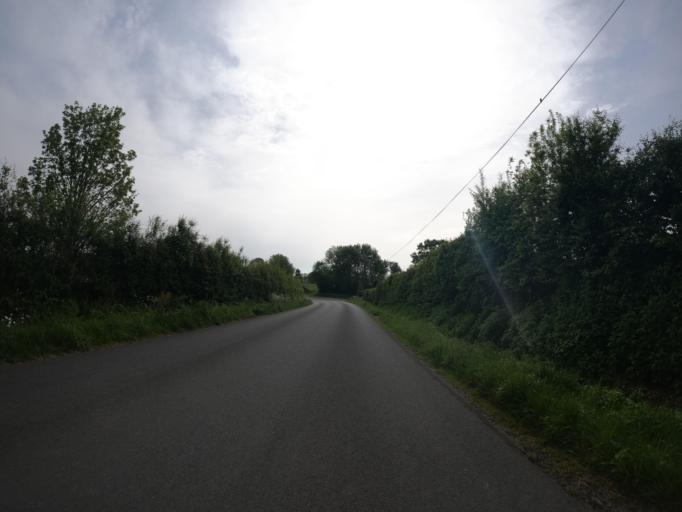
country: FR
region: Poitou-Charentes
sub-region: Departement des Deux-Sevres
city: La Chapelle-Saint-Laurent
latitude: 46.6943
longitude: -0.5115
